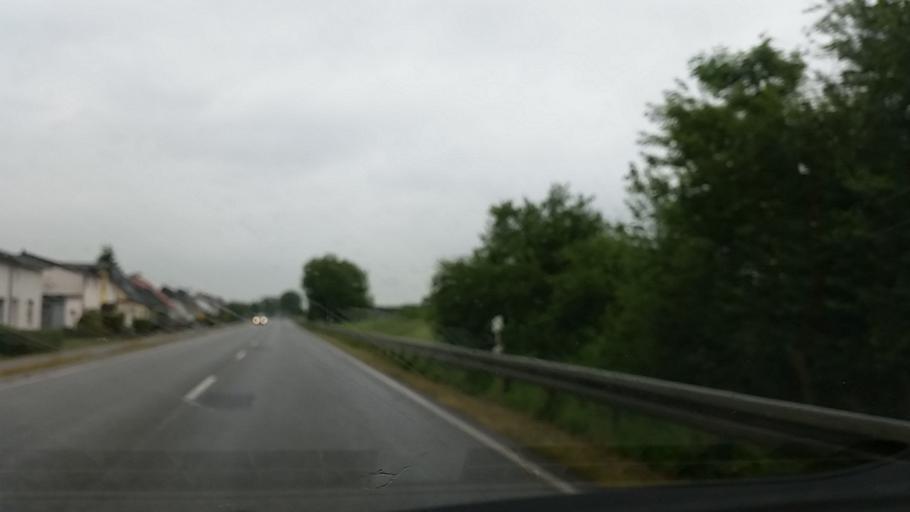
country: DE
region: Mecklenburg-Vorpommern
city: Biendorf
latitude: 54.0460
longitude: 11.7142
